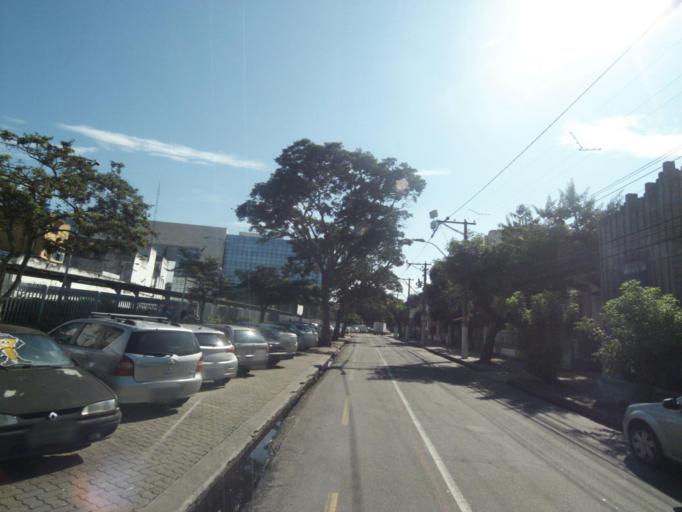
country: BR
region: Rio de Janeiro
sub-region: Niteroi
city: Niteroi
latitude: -22.8993
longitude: -43.1300
